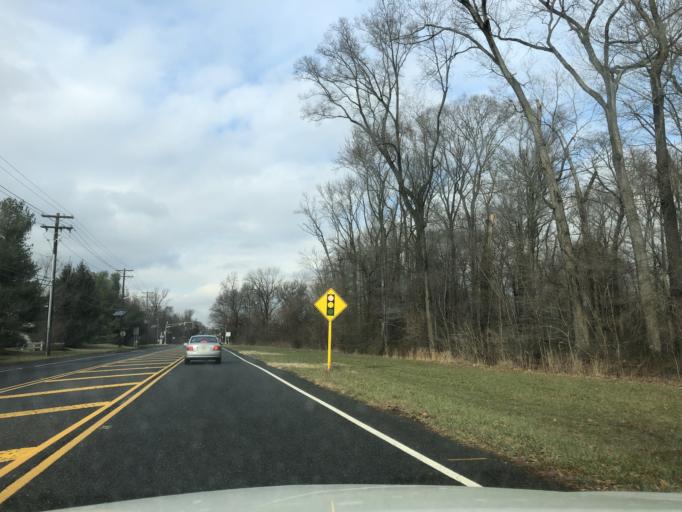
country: US
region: New Jersey
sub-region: Camden County
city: Bellmawr
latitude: 39.8461
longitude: -75.1052
